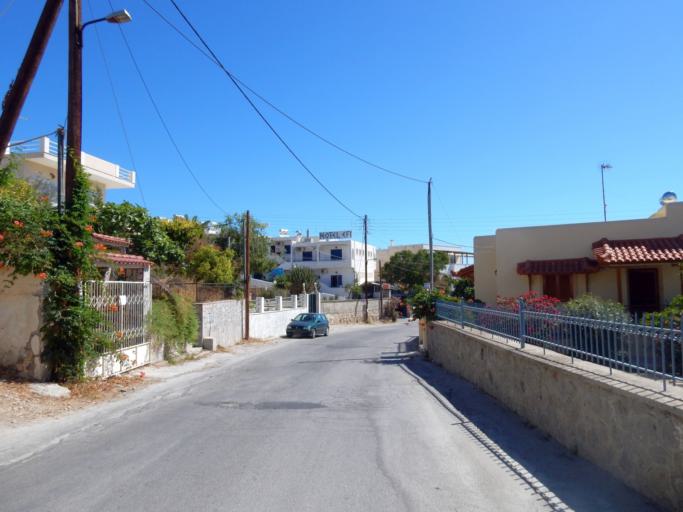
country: GR
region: Attica
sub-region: Nomos Piraios
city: Vathi
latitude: 37.7725
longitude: 23.4856
